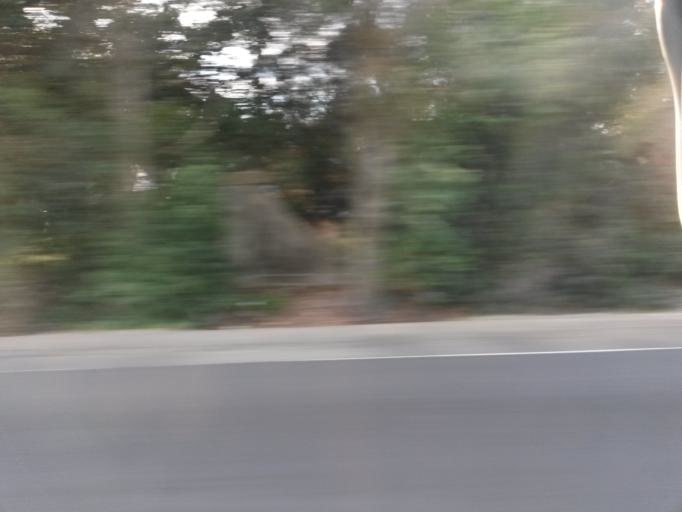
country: US
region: Louisiana
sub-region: Lafayette Parish
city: Lafayette
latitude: 30.2324
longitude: -92.0360
